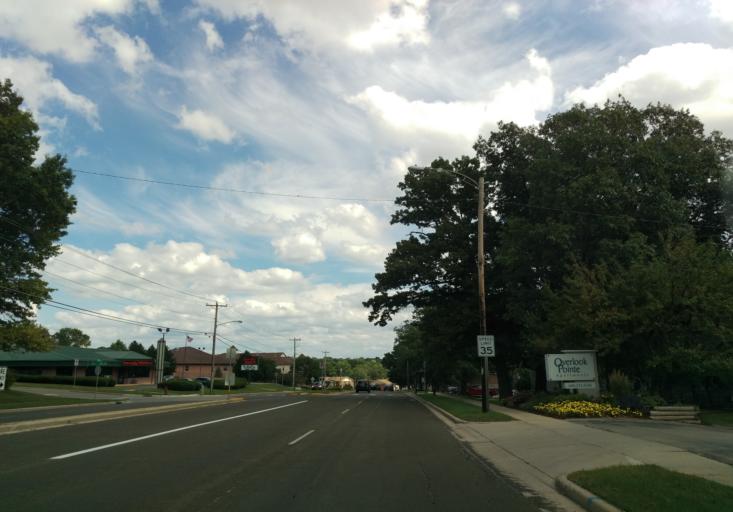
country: US
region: Wisconsin
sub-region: Dane County
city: Middleton
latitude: 43.1101
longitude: -89.4751
